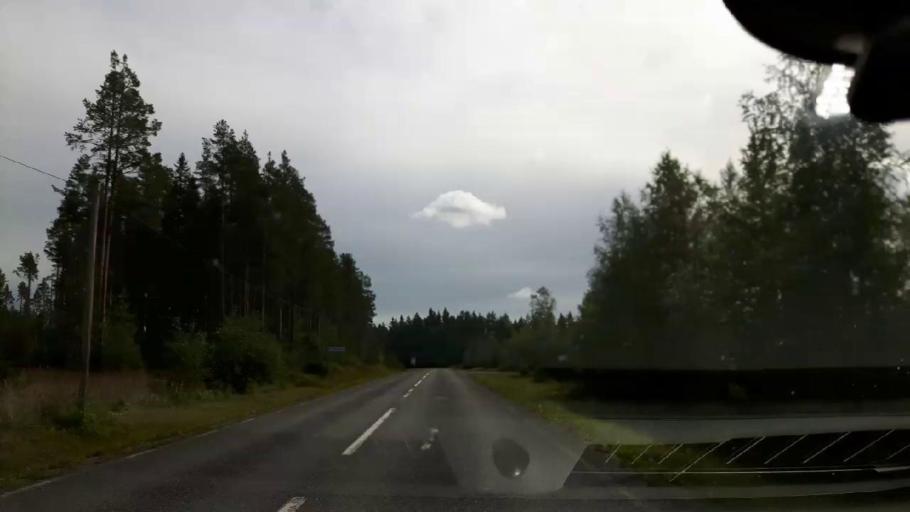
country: SE
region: Jaemtland
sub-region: Ragunda Kommun
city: Hammarstrand
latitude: 63.1412
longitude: 15.8613
